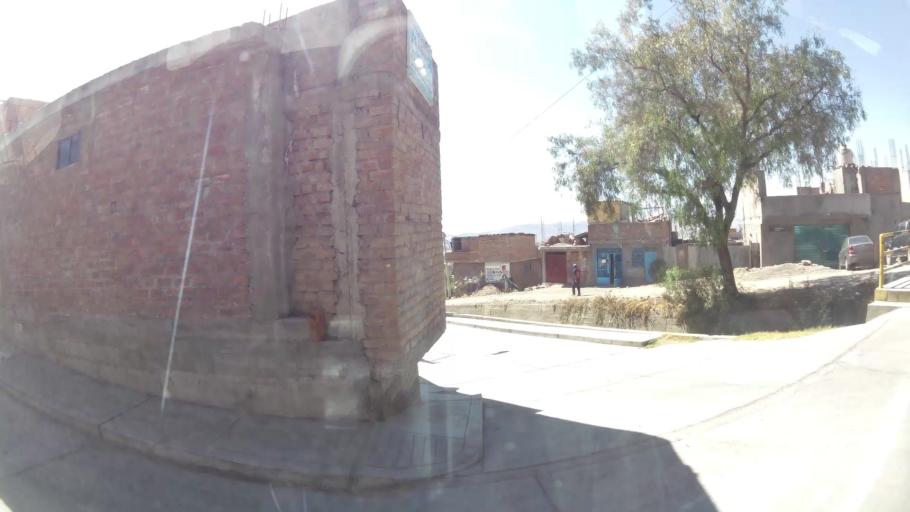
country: PE
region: Ayacucho
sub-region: Provincia de Huamanga
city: Ayacucho
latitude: -13.1543
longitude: -74.2328
